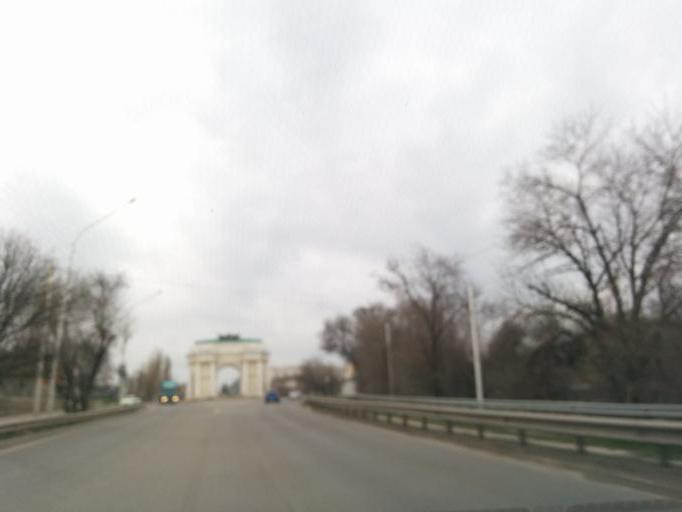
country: RU
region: Rostov
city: Novocherkassk
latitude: 47.4286
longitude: 40.0976
